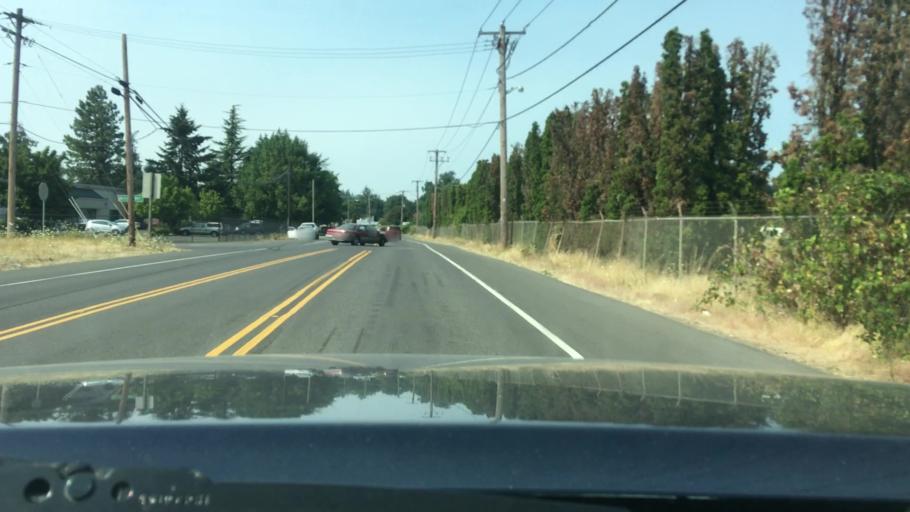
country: US
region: Oregon
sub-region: Lane County
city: Springfield
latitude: 44.0352
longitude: -123.0270
